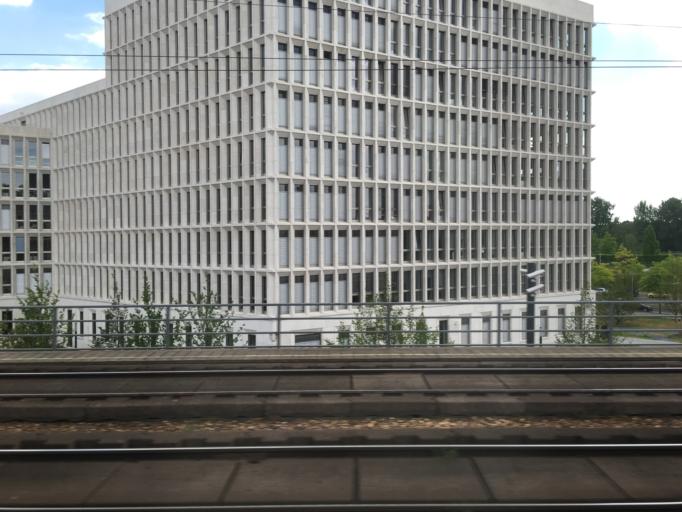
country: DE
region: Berlin
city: Tiergarten Bezirk
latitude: 52.5218
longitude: 13.3614
